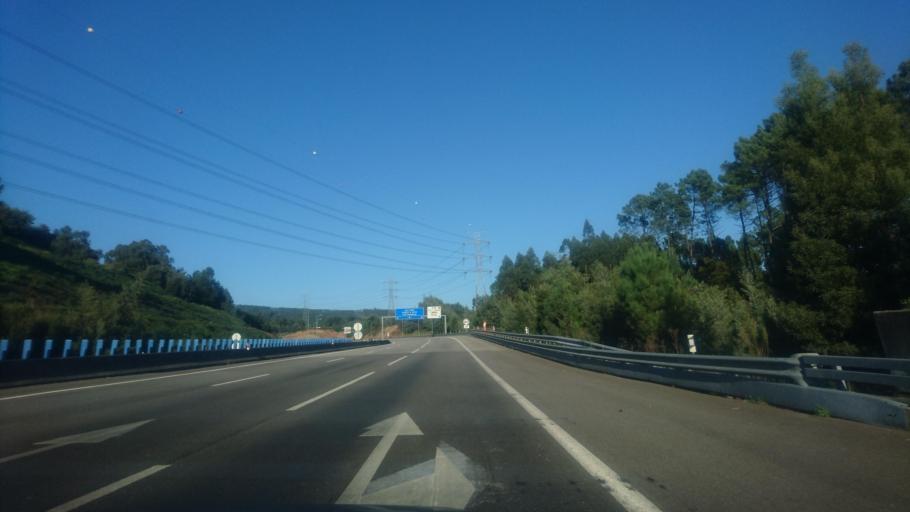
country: PT
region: Porto
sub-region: Gondomar
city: Foz do Sousa
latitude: 41.0643
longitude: -8.4557
